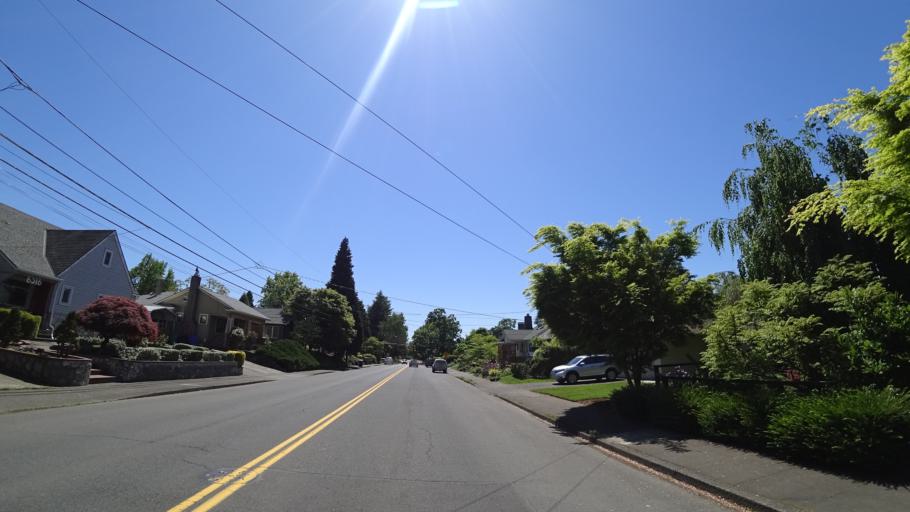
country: US
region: Oregon
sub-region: Clackamas County
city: Milwaukie
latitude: 45.4759
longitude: -122.6227
